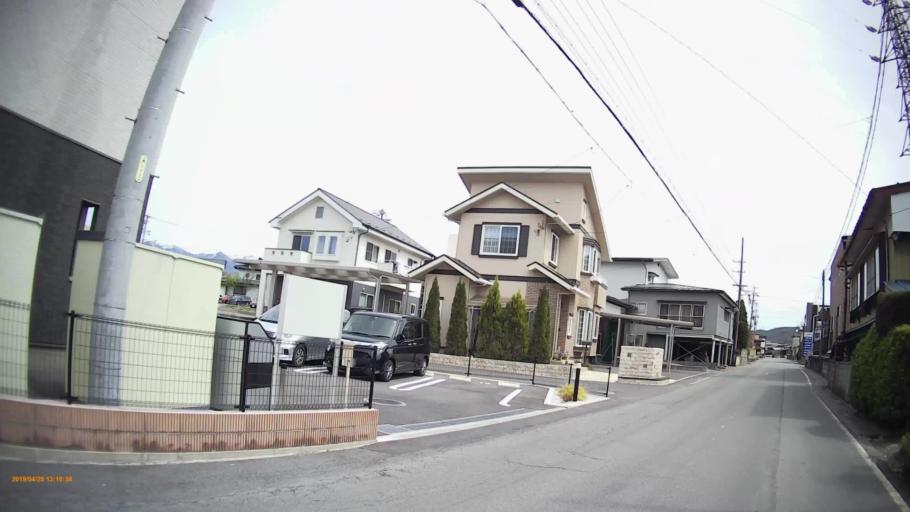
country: JP
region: Nagano
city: Chino
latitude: 35.9983
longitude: 138.1471
